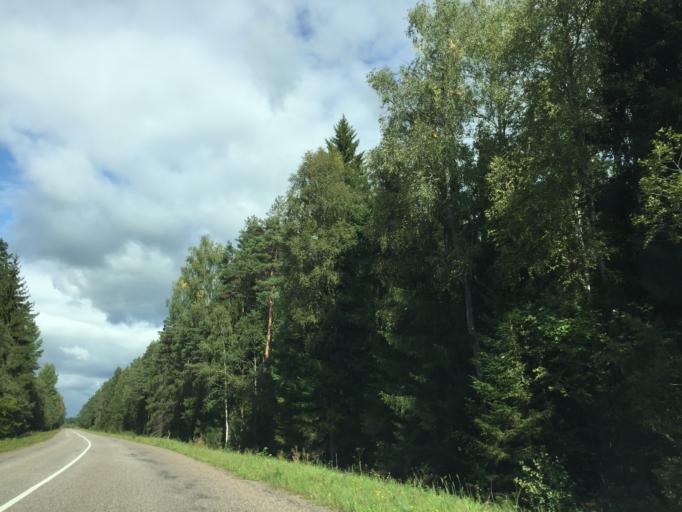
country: LV
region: Pargaujas
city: Stalbe
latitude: 57.4453
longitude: 24.9248
